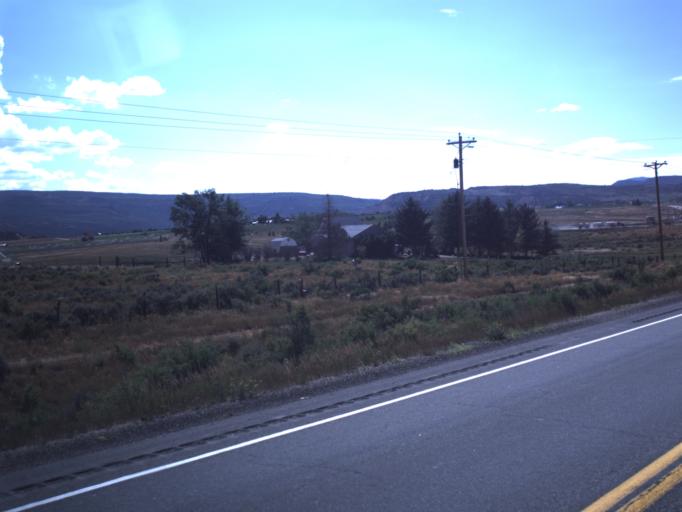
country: US
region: Utah
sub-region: Duchesne County
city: Duchesne
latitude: 40.2113
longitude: -110.8327
